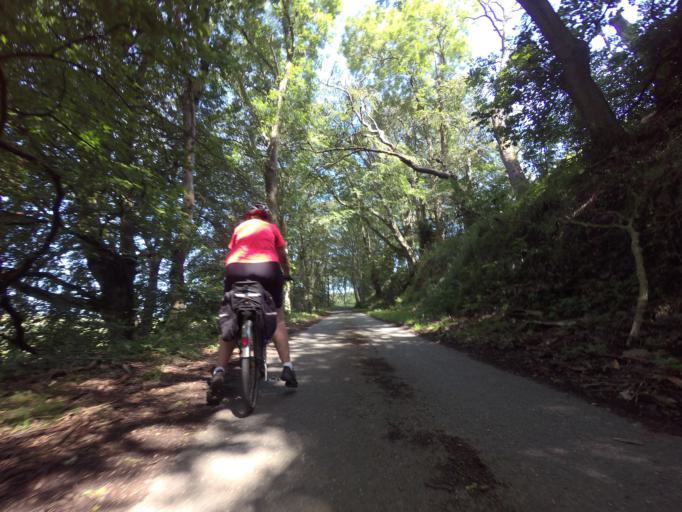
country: GB
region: Scotland
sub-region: Aberdeenshire
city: Banff
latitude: 57.6121
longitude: -2.5118
